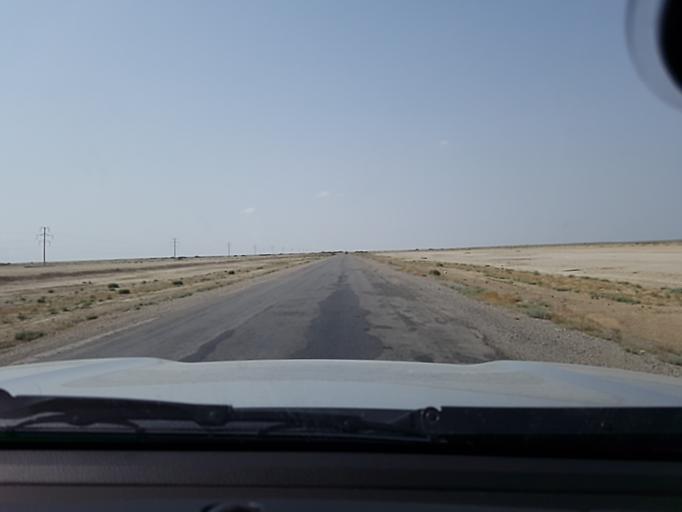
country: TM
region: Balkan
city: Gumdag
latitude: 38.9440
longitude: 54.5898
